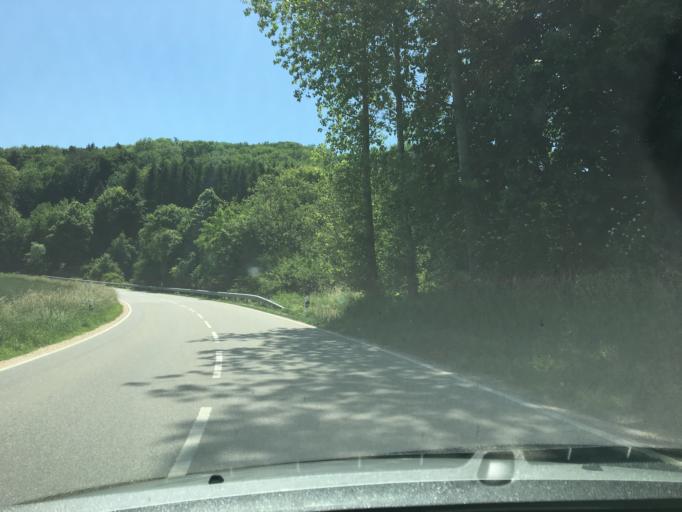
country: DE
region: Bavaria
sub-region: Upper Bavaria
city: Unterneukirchen
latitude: 48.1397
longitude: 12.6427
